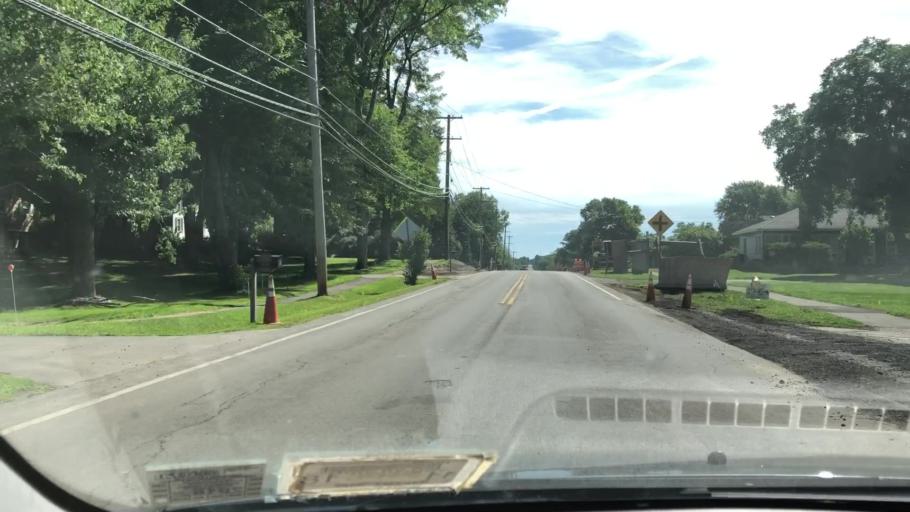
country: US
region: New York
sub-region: Monroe County
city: Fairport
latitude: 43.1084
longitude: -77.4176
